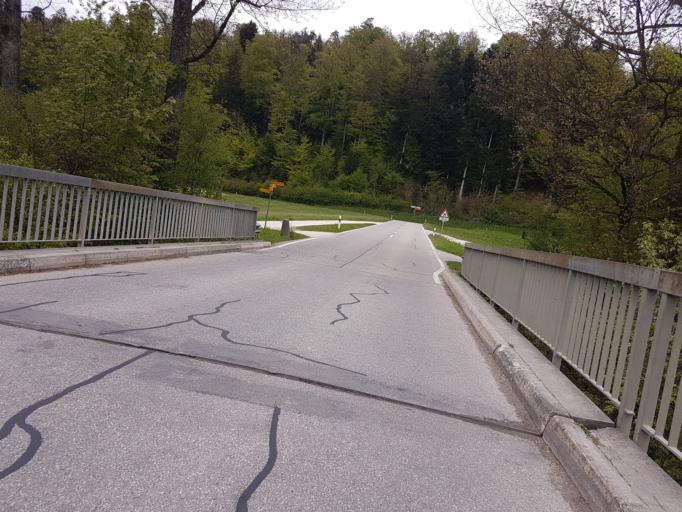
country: CH
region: Bern
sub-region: Oberaargau
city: Niederbipp
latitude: 47.2314
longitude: 7.7065
